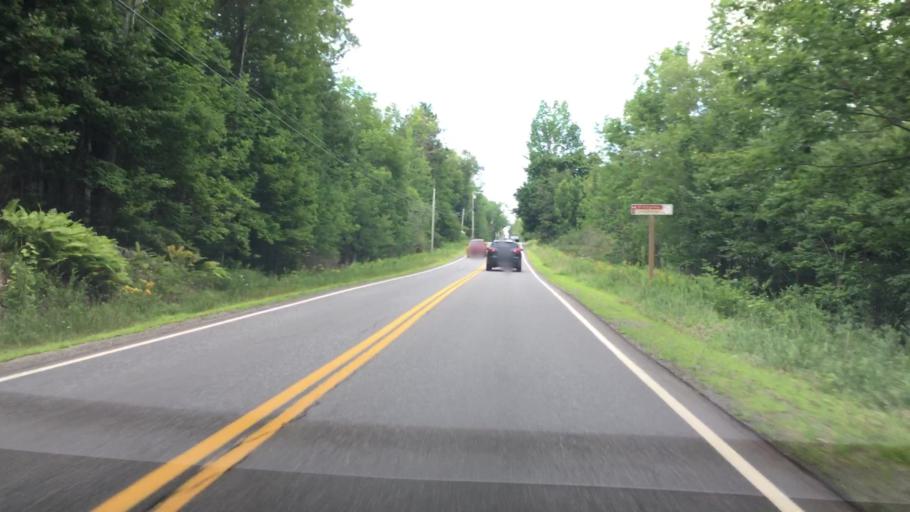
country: US
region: Maine
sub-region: Waldo County
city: Lincolnville
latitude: 44.3526
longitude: -69.0533
